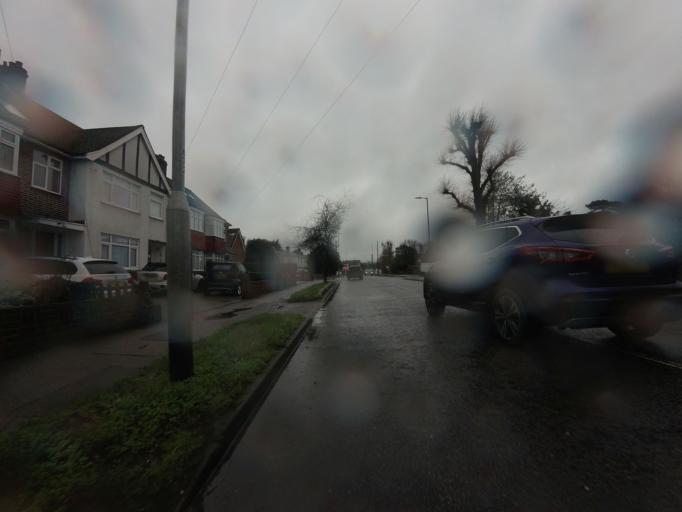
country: GB
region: England
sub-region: Hertfordshire
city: Cheshunt
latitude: 51.7106
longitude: -0.0495
